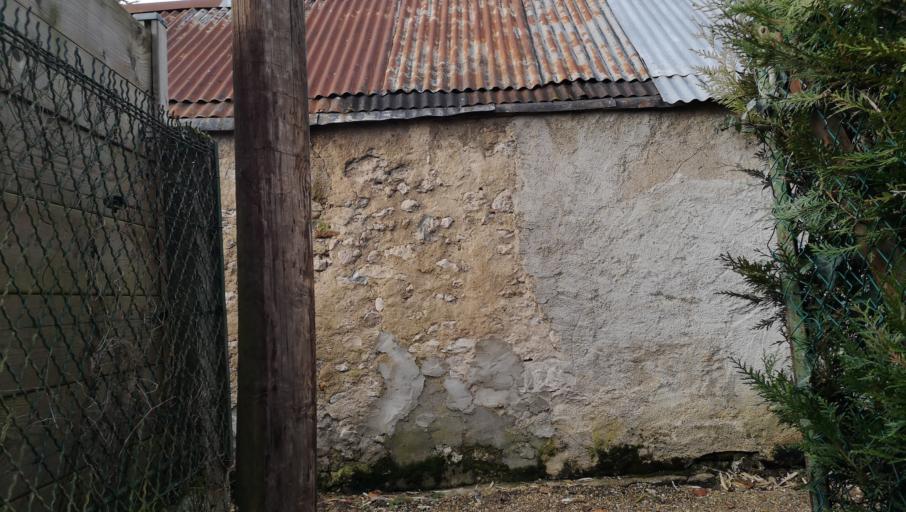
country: FR
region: Centre
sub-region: Departement du Loiret
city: Saint-Jean-le-Blanc
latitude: 47.9062
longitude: 1.9291
